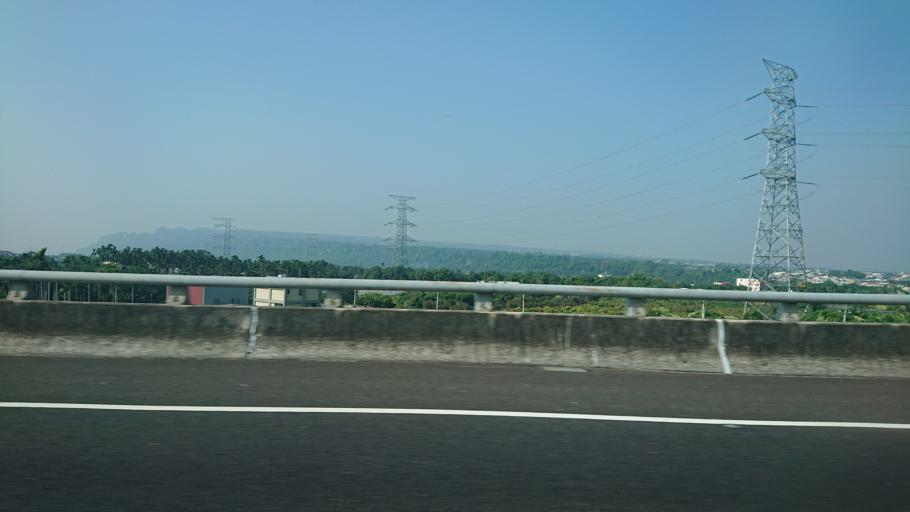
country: TW
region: Taiwan
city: Lugu
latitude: 23.8305
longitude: 120.7084
